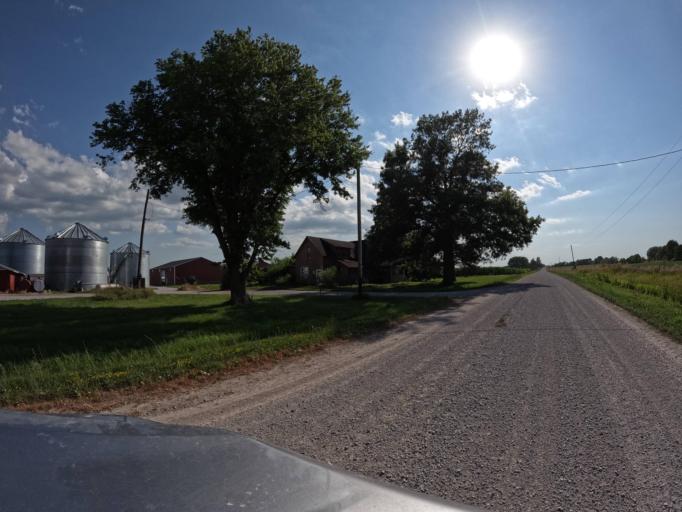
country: US
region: Iowa
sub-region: Appanoose County
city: Centerville
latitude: 40.7179
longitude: -93.0436
